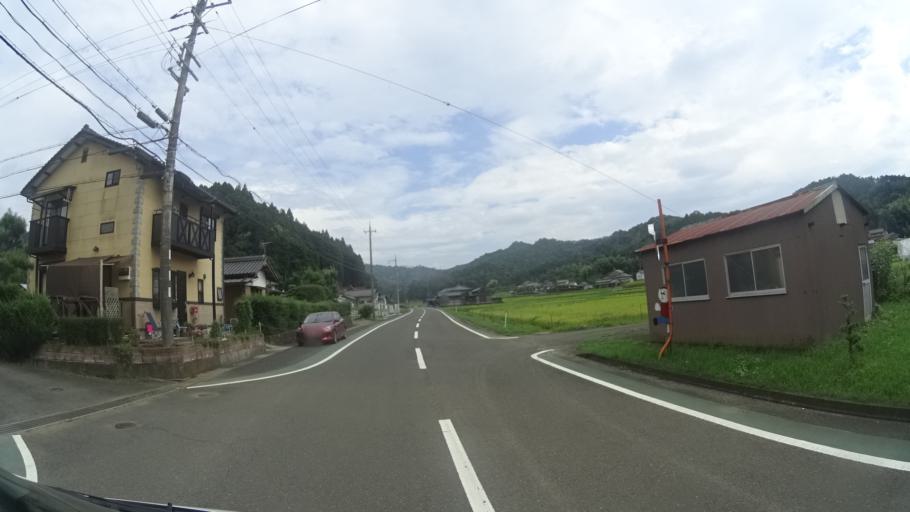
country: JP
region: Kyoto
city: Ayabe
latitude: 35.3588
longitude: 135.3207
